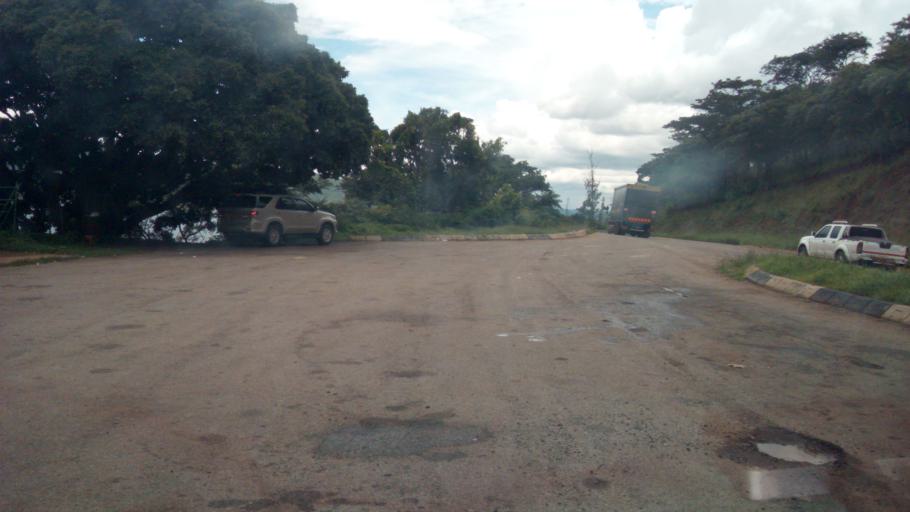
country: ZW
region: Mashonaland Central
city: Mazowe
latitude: -17.5220
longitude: 30.9882
